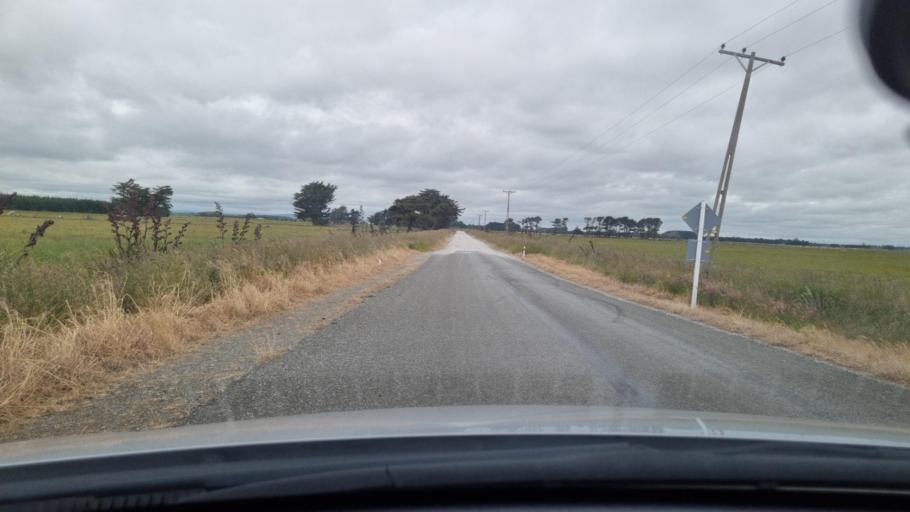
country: NZ
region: Southland
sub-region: Invercargill City
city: Invercargill
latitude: -46.3909
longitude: 168.2752
